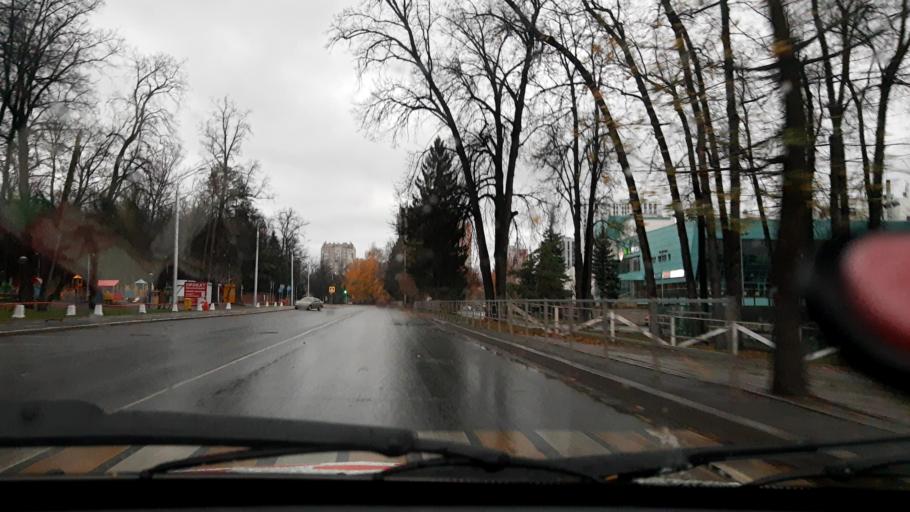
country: RU
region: Bashkortostan
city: Ufa
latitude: 54.7742
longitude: 56.0187
